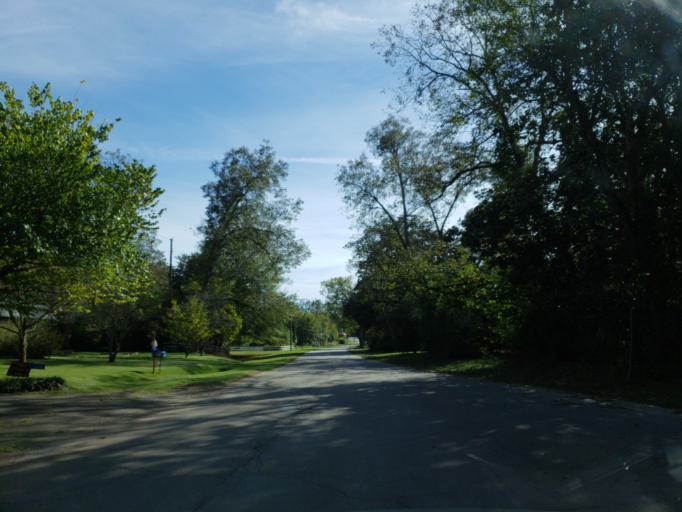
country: US
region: Georgia
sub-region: Crawford County
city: Roberta
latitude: 32.8671
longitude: -84.0927
